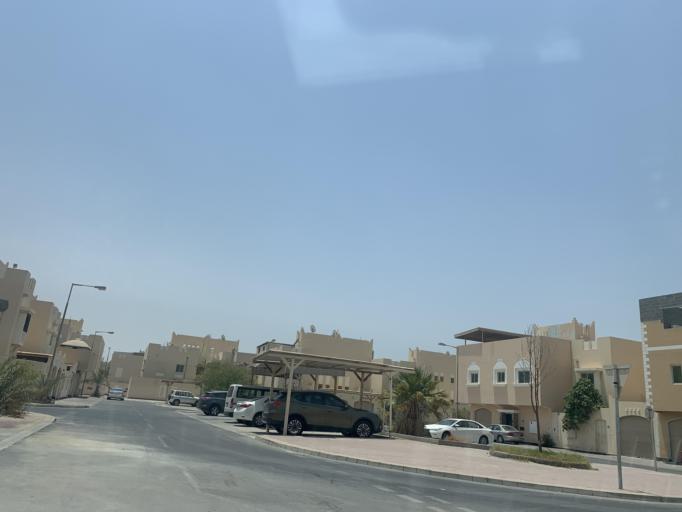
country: BH
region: Manama
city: Jidd Hafs
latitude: 26.2109
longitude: 50.4713
